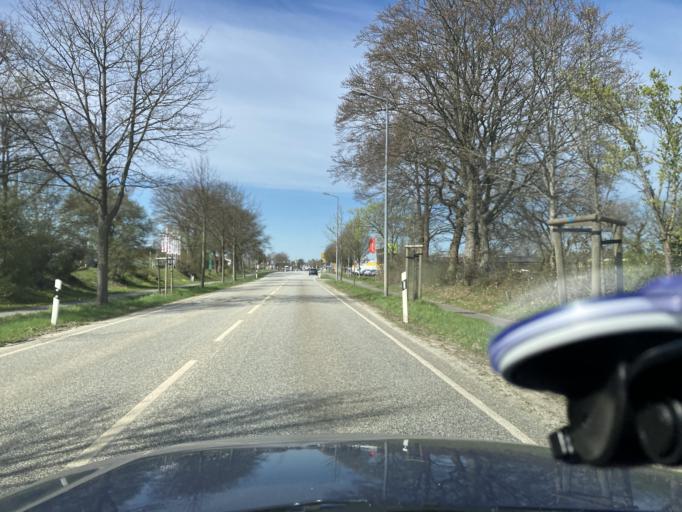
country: DE
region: Schleswig-Holstein
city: Ostrohe
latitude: 54.1976
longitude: 9.1299
